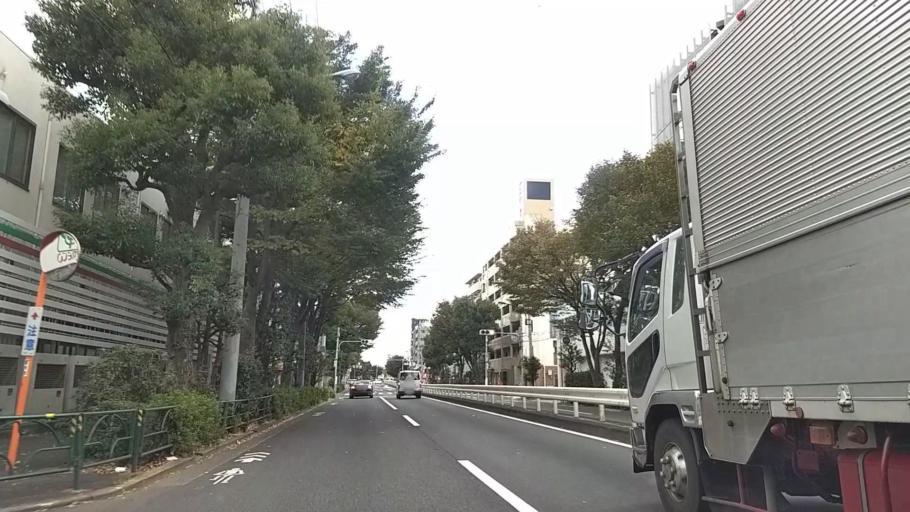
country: JP
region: Tokyo
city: Tokyo
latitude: 35.6102
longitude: 139.6915
